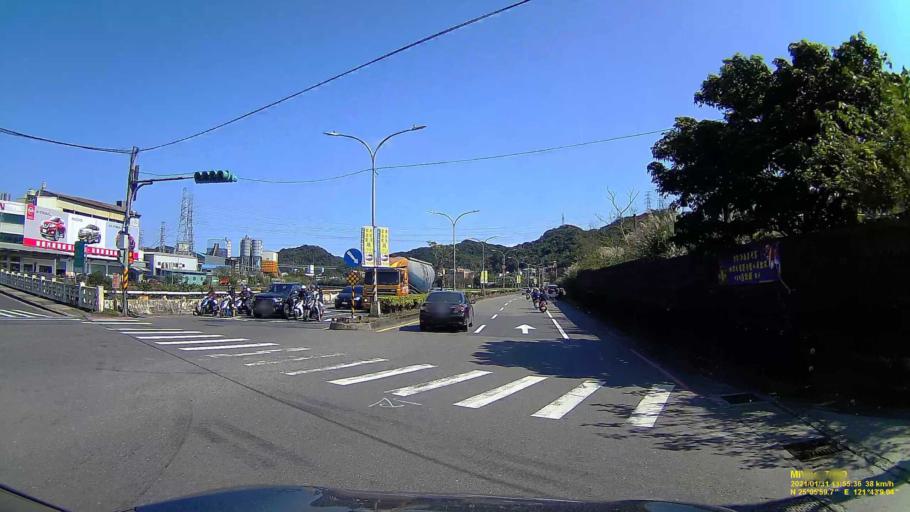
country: TW
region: Taiwan
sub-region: Keelung
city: Keelung
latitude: 25.1001
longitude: 121.7192
